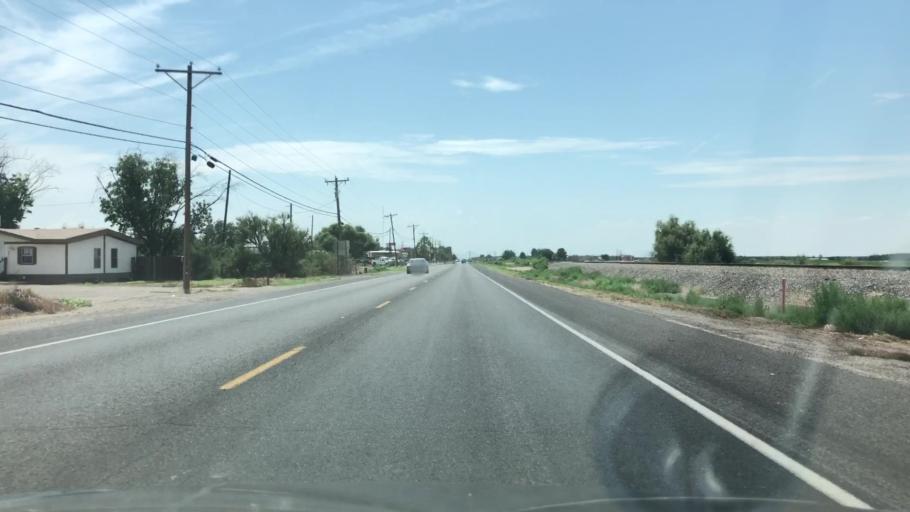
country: US
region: New Mexico
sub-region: Dona Ana County
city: University Park
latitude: 32.2468
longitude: -106.7485
